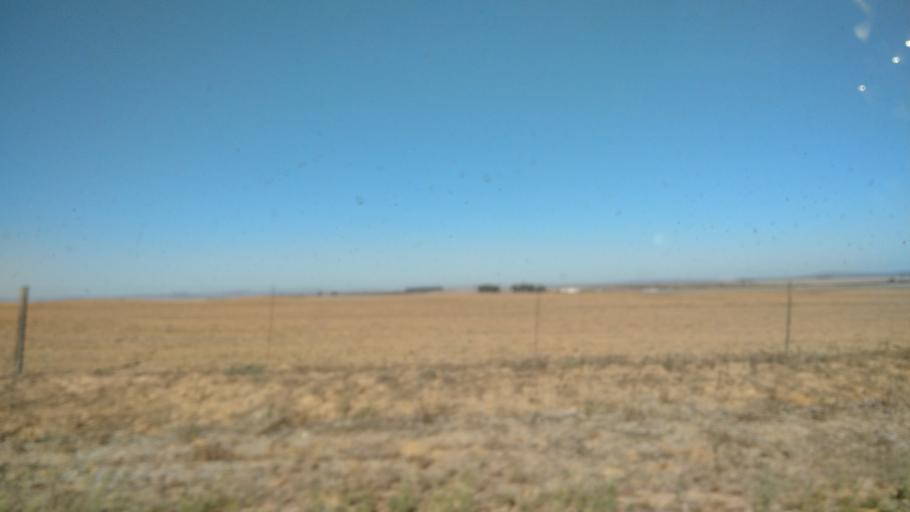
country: ZA
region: Western Cape
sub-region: West Coast District Municipality
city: Moorreesburg
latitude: -33.1763
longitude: 18.4878
